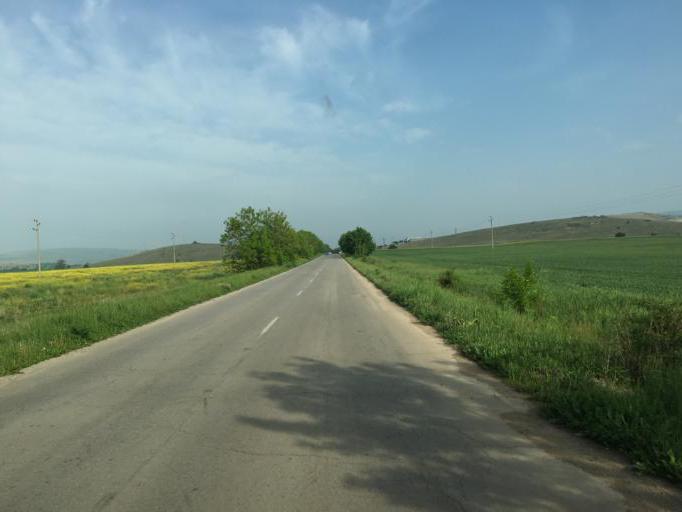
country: BG
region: Pernik
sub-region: Obshtina Radomir
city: Radomir
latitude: 42.4921
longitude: 23.0419
